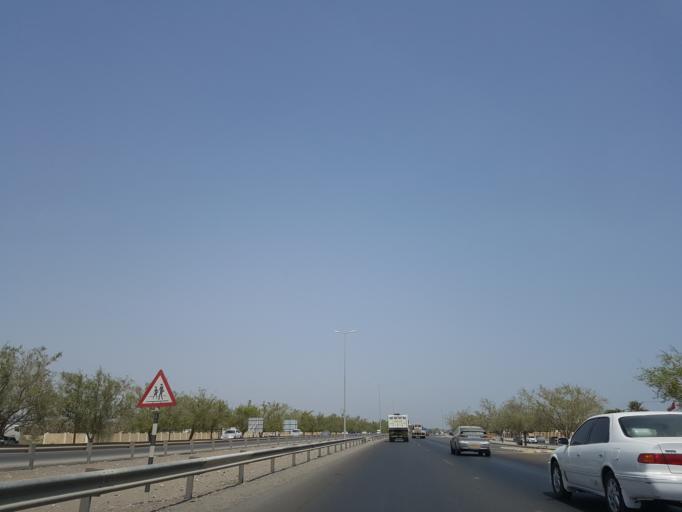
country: OM
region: Al Batinah
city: Saham
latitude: 24.1462
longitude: 56.8725
